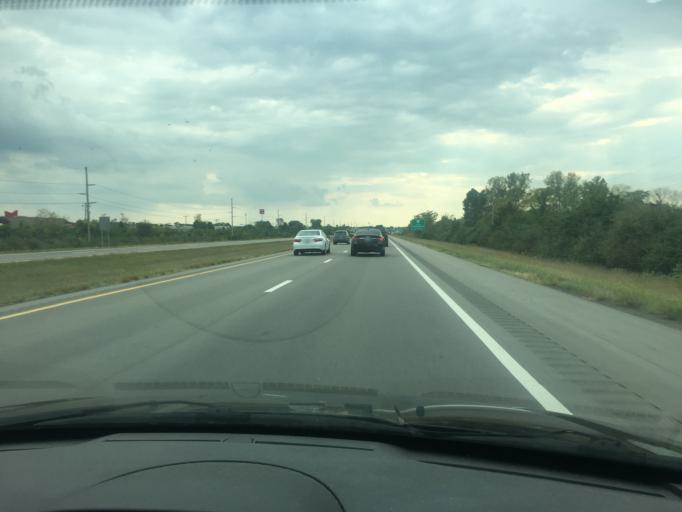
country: US
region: Ohio
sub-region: Clark County
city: Springfield
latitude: 39.9524
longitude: -83.8323
